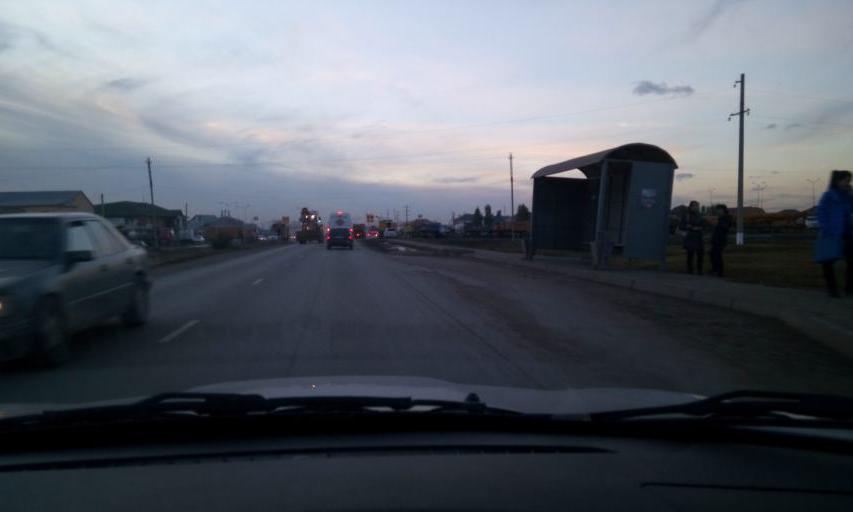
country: KZ
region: Astana Qalasy
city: Astana
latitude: 51.1362
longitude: 71.5245
